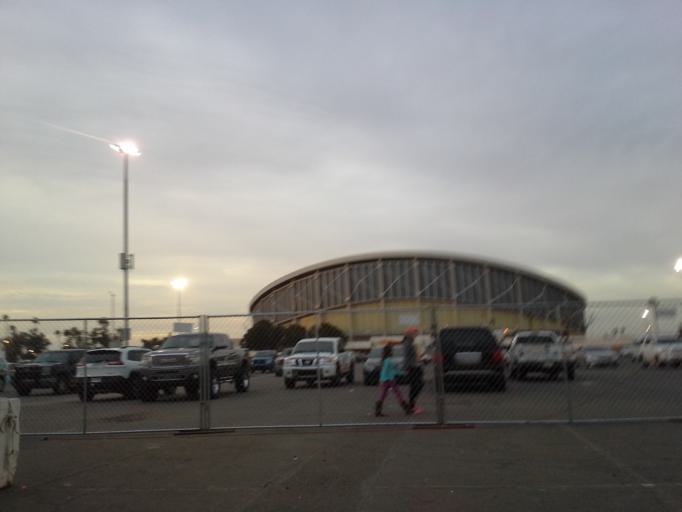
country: US
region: Arizona
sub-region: Maricopa County
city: Phoenix
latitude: 33.4674
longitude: -112.0965
